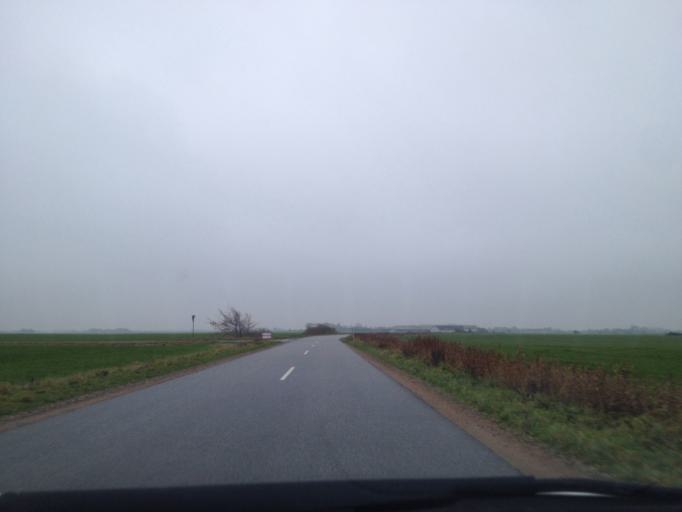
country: DK
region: South Denmark
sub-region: Tonder Kommune
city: Sherrebek
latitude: 55.1018
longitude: 8.7276
